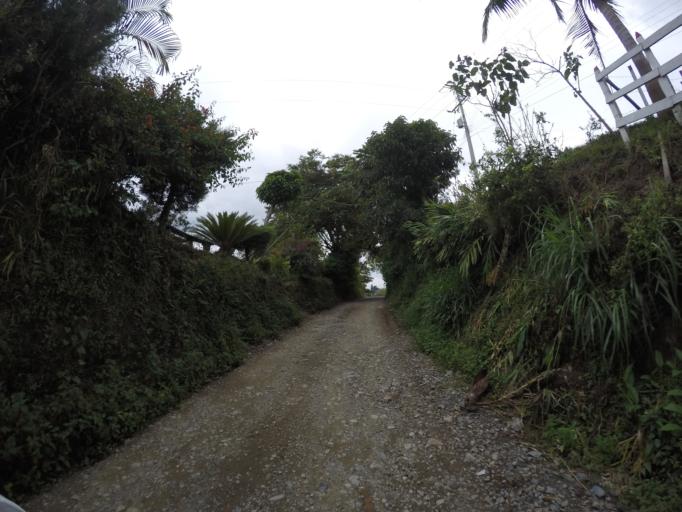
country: CO
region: Quindio
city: Filandia
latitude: 4.6405
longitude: -75.6782
